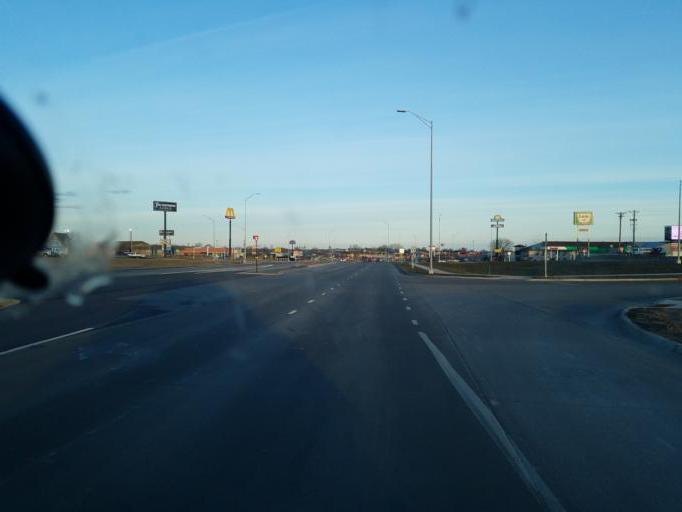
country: US
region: South Dakota
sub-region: Davison County
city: Mitchell
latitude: 43.6936
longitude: -98.0134
